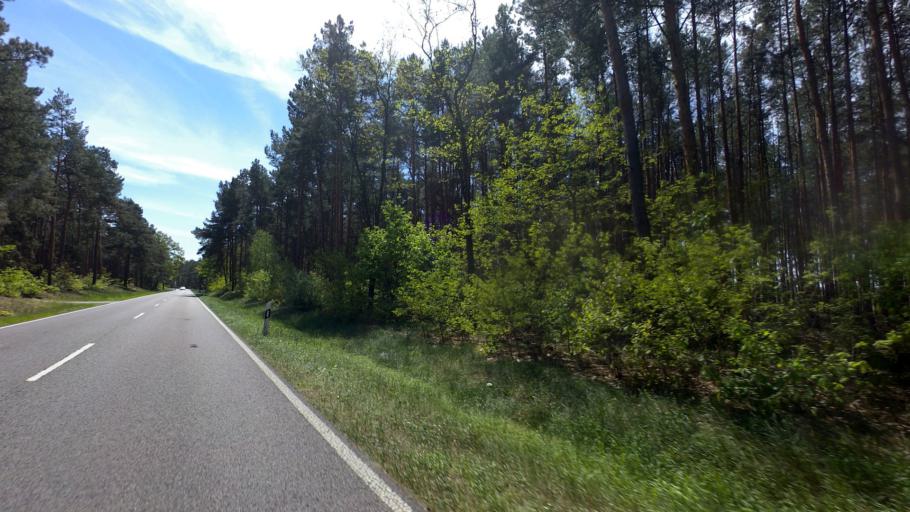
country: DE
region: Brandenburg
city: Luckenwalde
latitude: 52.1464
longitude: 13.1137
